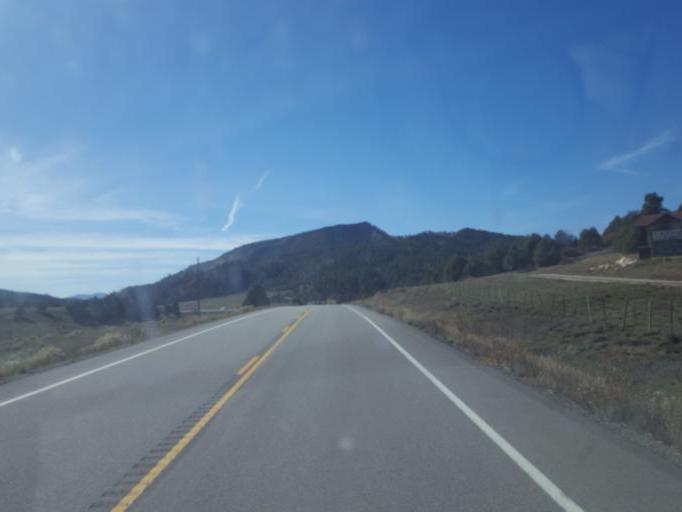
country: US
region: Colorado
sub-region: Archuleta County
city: Pagosa Springs
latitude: 37.2292
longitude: -107.2045
